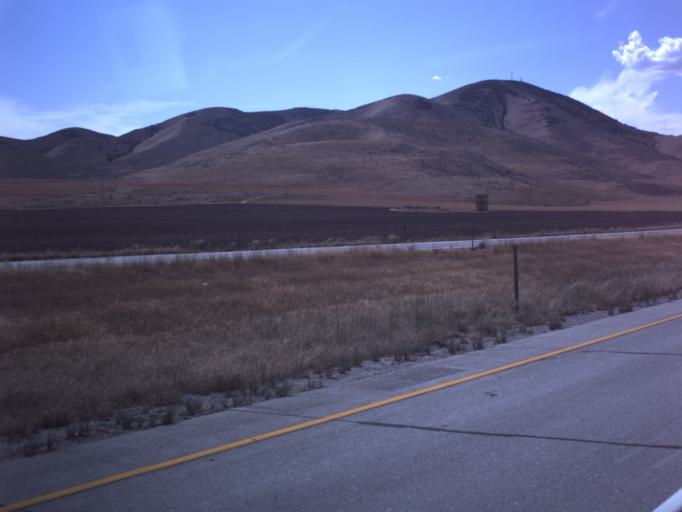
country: US
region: Utah
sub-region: Box Elder County
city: Garland
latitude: 41.7952
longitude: -112.2886
